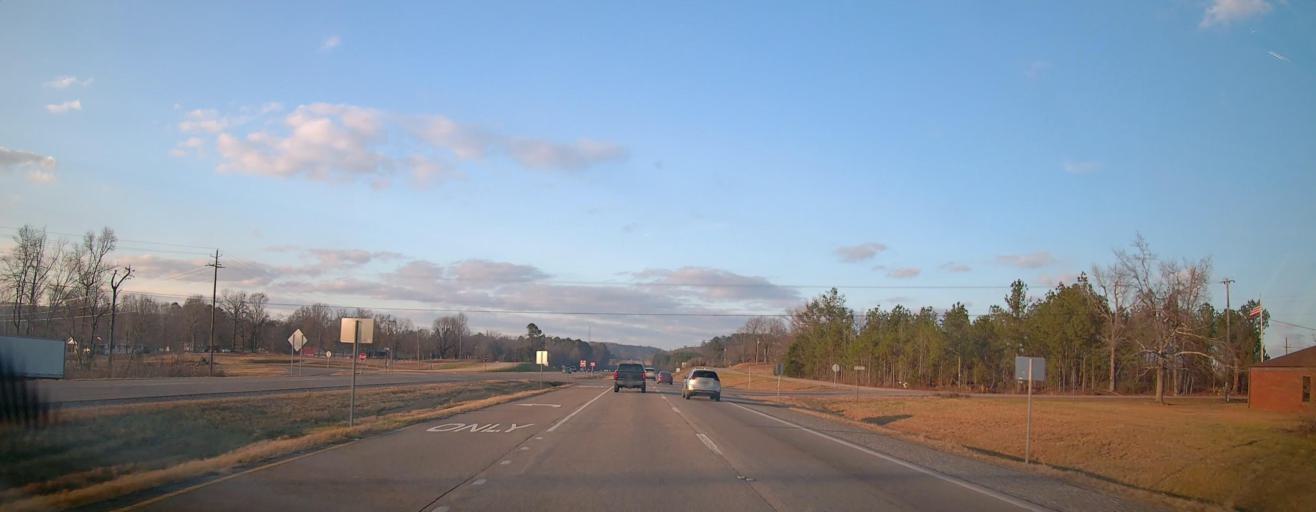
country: US
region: Alabama
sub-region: Calhoun County
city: Alexandria
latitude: 33.8220
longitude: -85.9081
